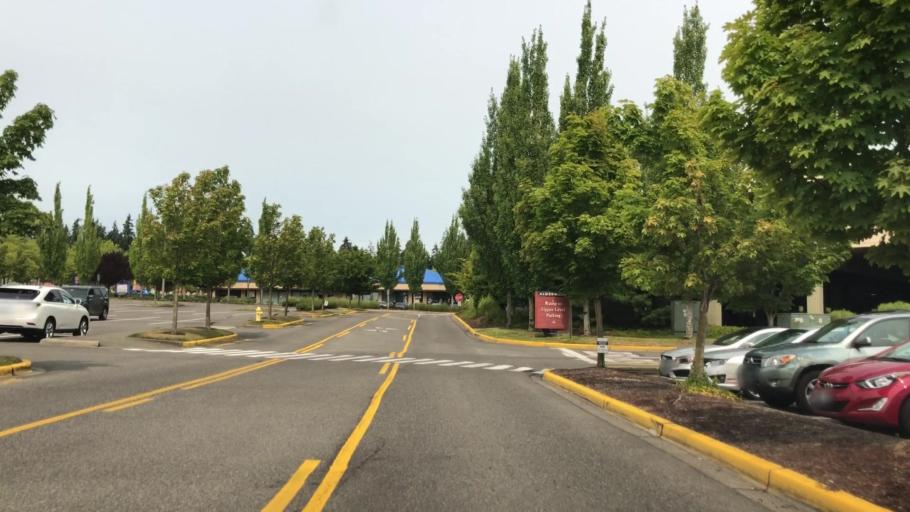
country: US
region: Washington
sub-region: Snohomish County
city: Alderwood Manor
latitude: 47.8299
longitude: -122.2768
